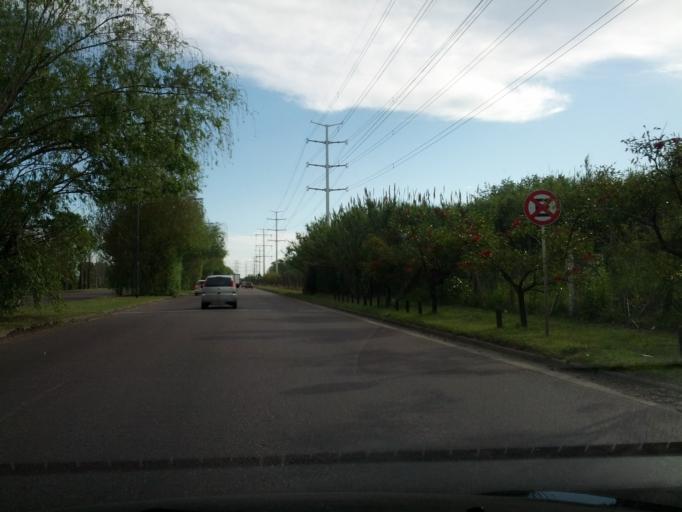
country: AR
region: Buenos Aires F.D.
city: Villa Lugano
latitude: -34.6973
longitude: -58.4549
